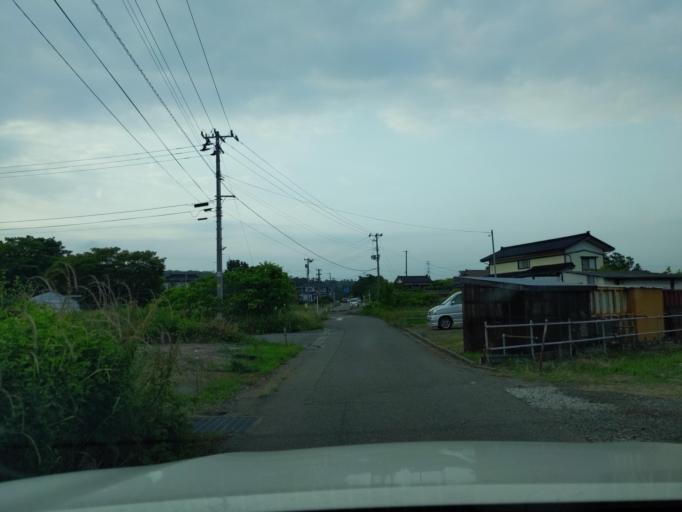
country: JP
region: Niigata
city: Kashiwazaki
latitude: 37.4019
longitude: 138.6002
